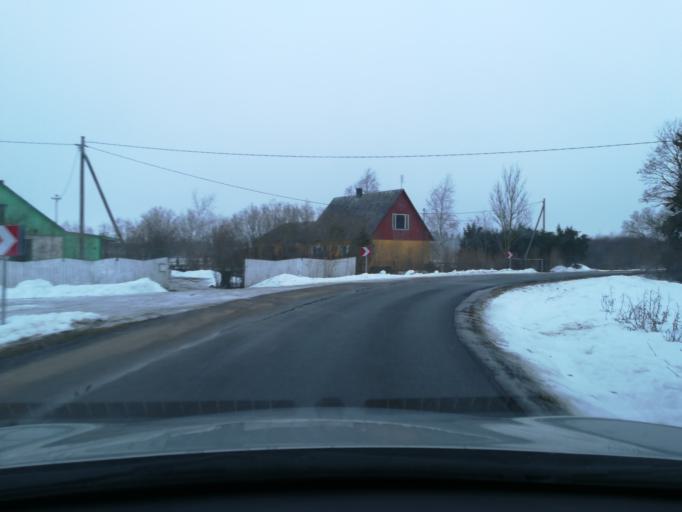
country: EE
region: Harju
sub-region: Raasiku vald
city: Raasiku
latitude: 59.3375
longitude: 25.2384
